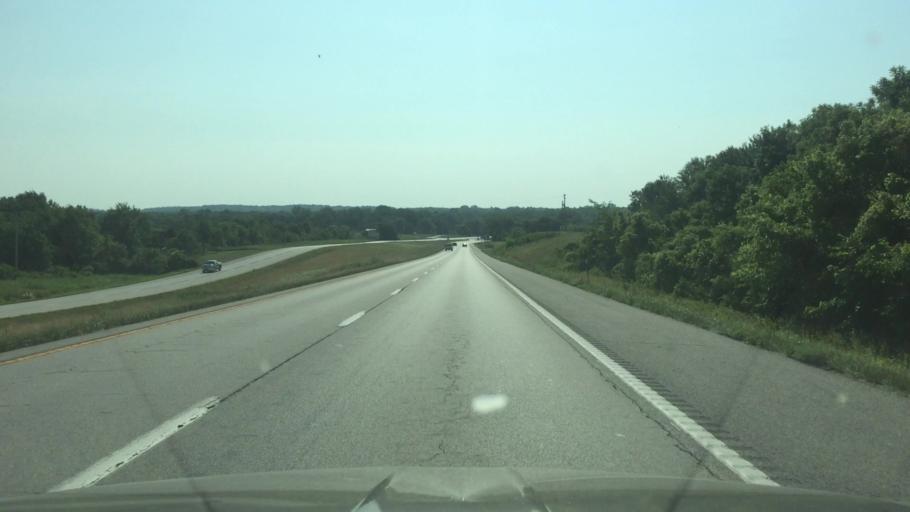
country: US
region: Missouri
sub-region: Jackson County
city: Lone Jack
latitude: 38.8730
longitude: -94.1419
